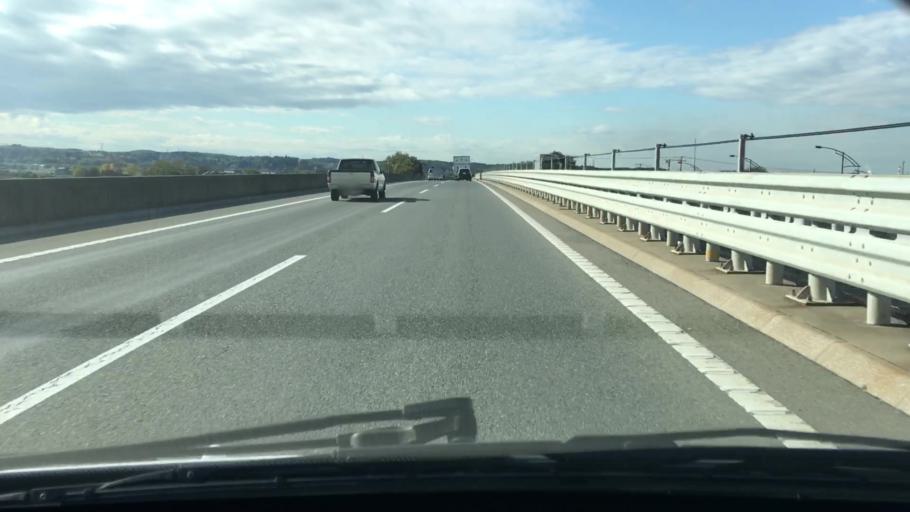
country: JP
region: Chiba
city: Ichihara
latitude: 35.4909
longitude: 140.0876
